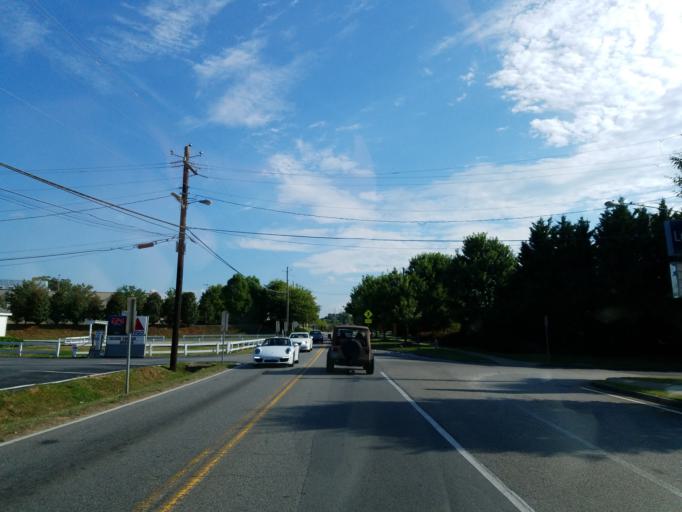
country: US
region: Georgia
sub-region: Fulton County
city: Roswell
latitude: 34.0809
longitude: -84.3578
